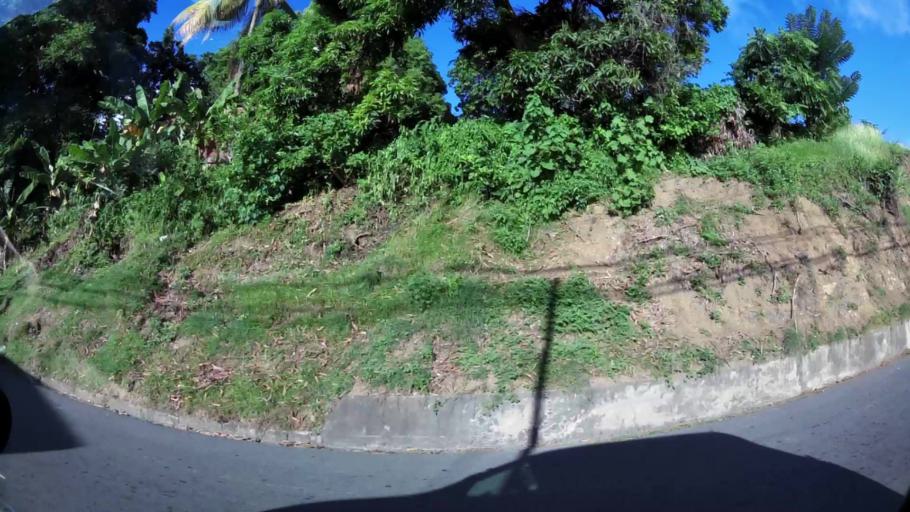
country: TT
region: Tobago
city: Scarborough
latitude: 11.1922
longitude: -60.6832
